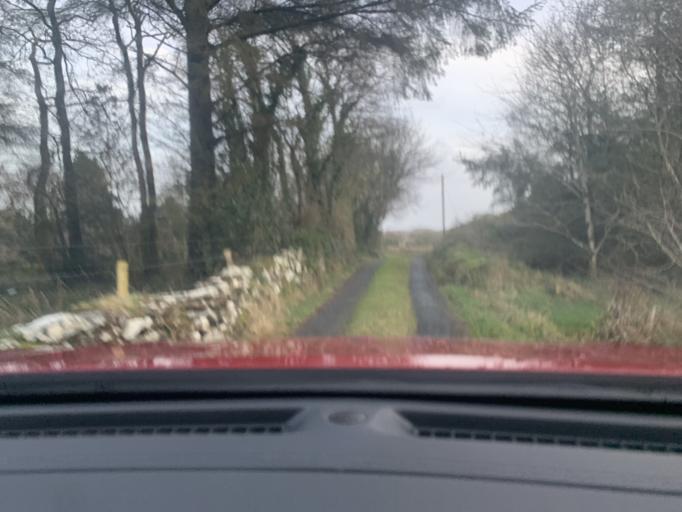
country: IE
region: Connaught
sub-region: Roscommon
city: Ballaghaderreen
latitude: 53.9542
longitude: -8.5403
